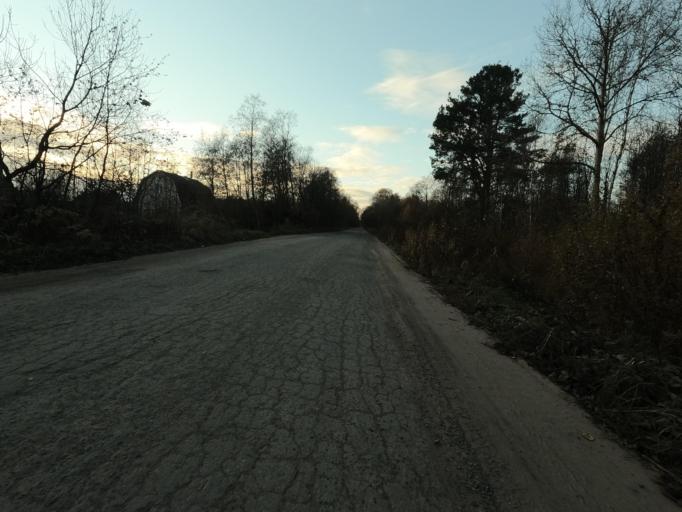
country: RU
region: Leningrad
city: Mga
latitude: 59.7655
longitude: 31.2451
